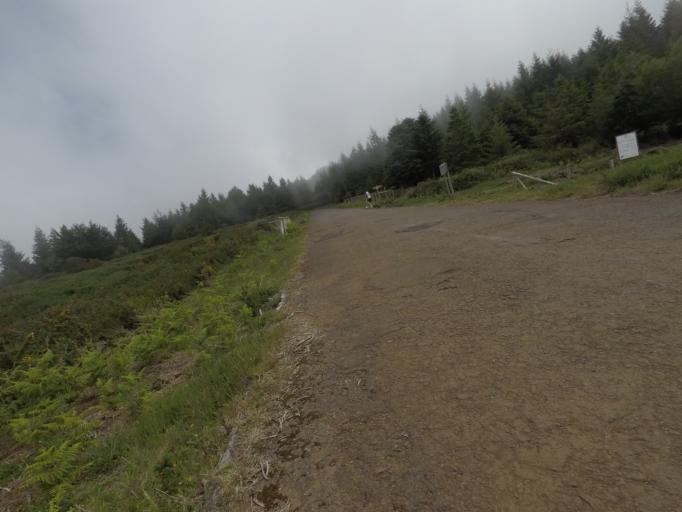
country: PT
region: Madeira
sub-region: Sao Vicente
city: Sao Vicente
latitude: 32.7699
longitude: -17.0785
